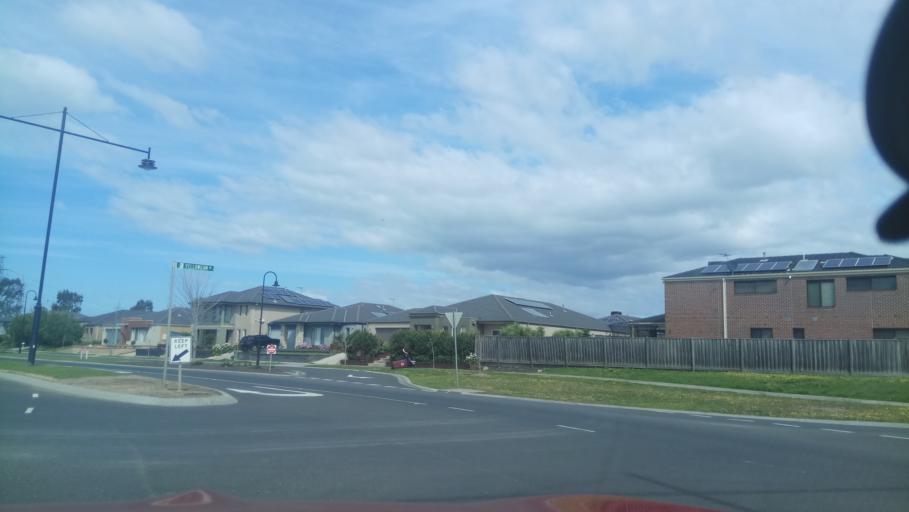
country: AU
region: Victoria
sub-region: Casey
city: Lynbrook
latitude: -38.0765
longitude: 145.2568
